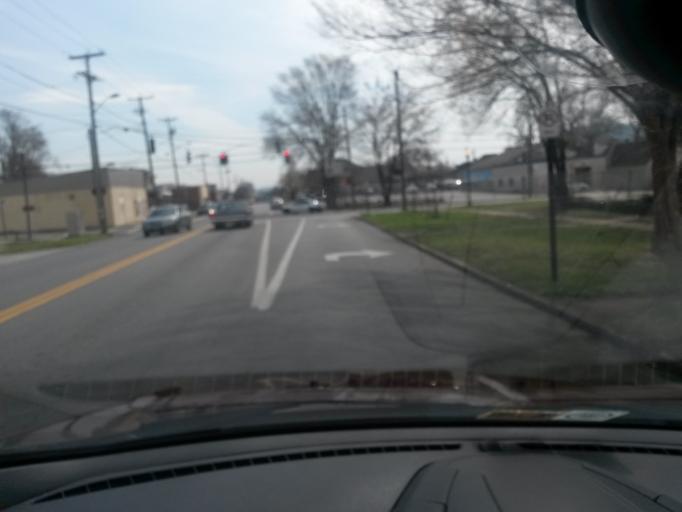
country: US
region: Virginia
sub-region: City of Roanoke
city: Roanoke
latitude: 37.2725
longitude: -79.9640
